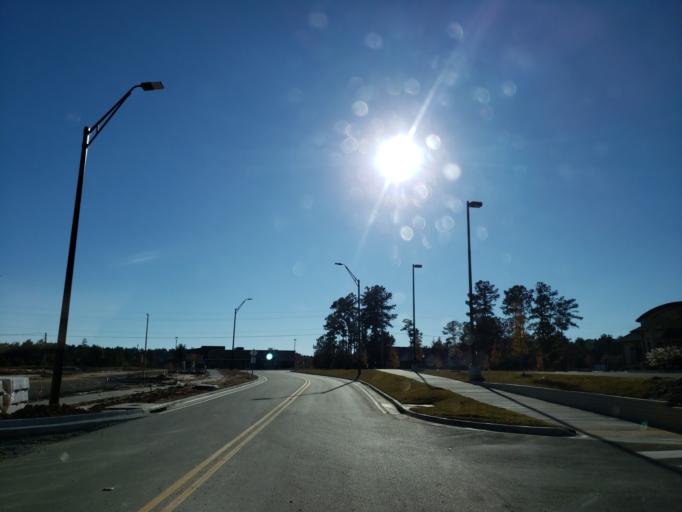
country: US
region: Mississippi
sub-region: Forrest County
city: Hattiesburg
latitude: 31.2818
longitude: -89.3233
